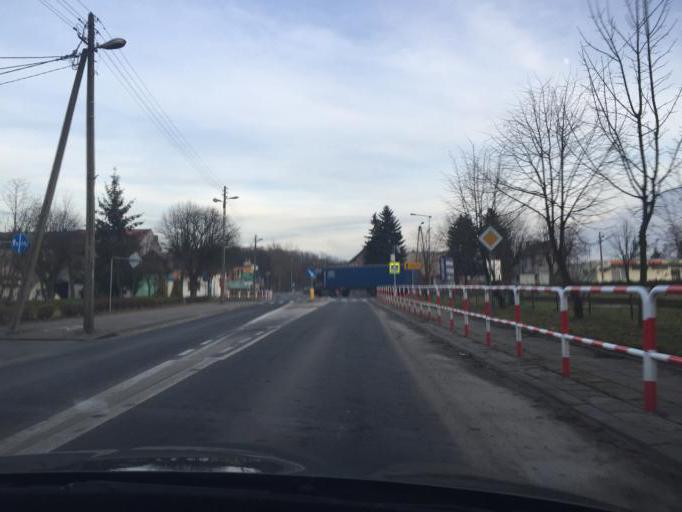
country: PL
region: Lubusz
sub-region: Powiat zielonogorski
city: Nowogrod Bobrzanski
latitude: 51.7985
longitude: 15.2339
